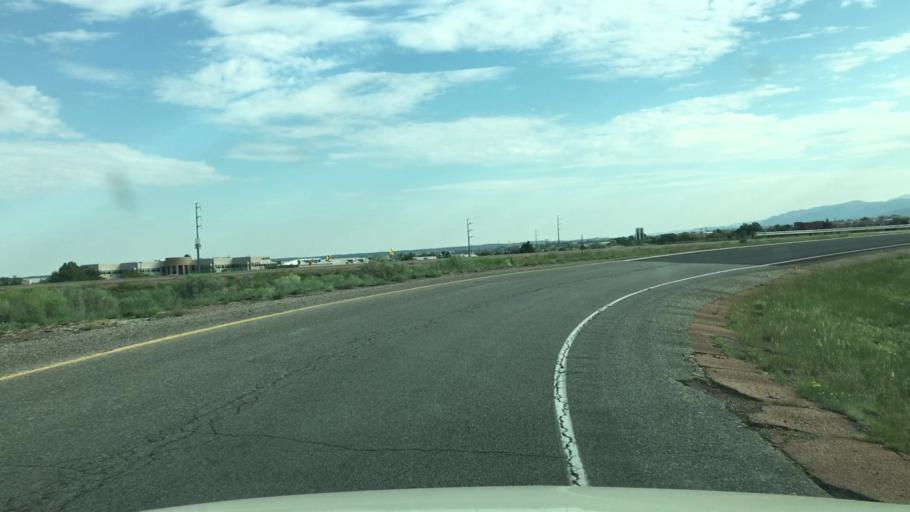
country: US
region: New Mexico
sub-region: Santa Fe County
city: Santa Fe
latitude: 35.6330
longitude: -105.9582
